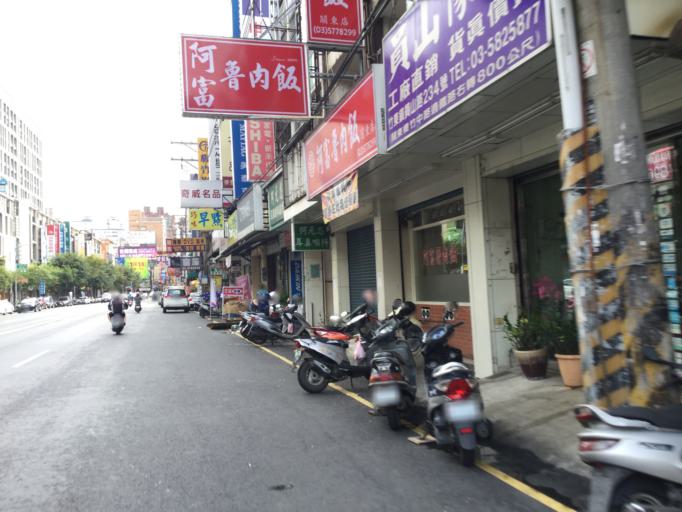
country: TW
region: Taiwan
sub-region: Hsinchu
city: Hsinchu
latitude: 24.7841
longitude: 121.0157
